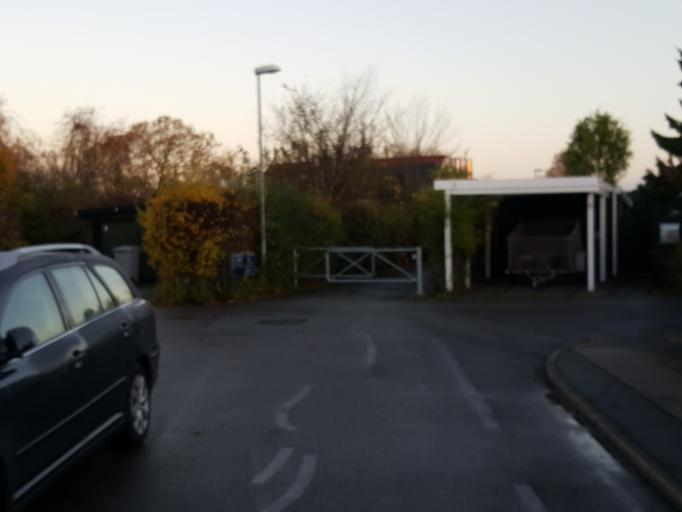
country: DK
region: Capital Region
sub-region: Tarnby Kommune
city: Tarnby
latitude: 55.6167
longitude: 12.5796
